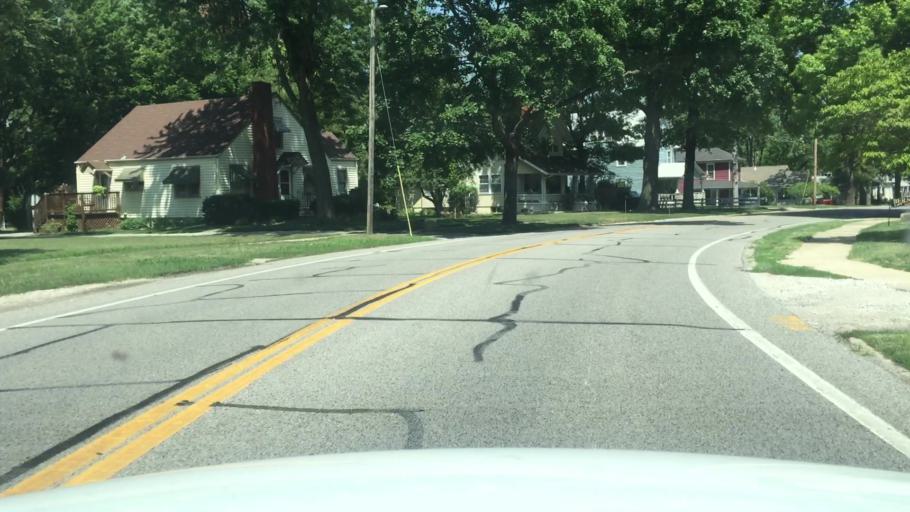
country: US
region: Missouri
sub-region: Jackson County
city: Lees Summit
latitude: 38.9180
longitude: -94.3800
